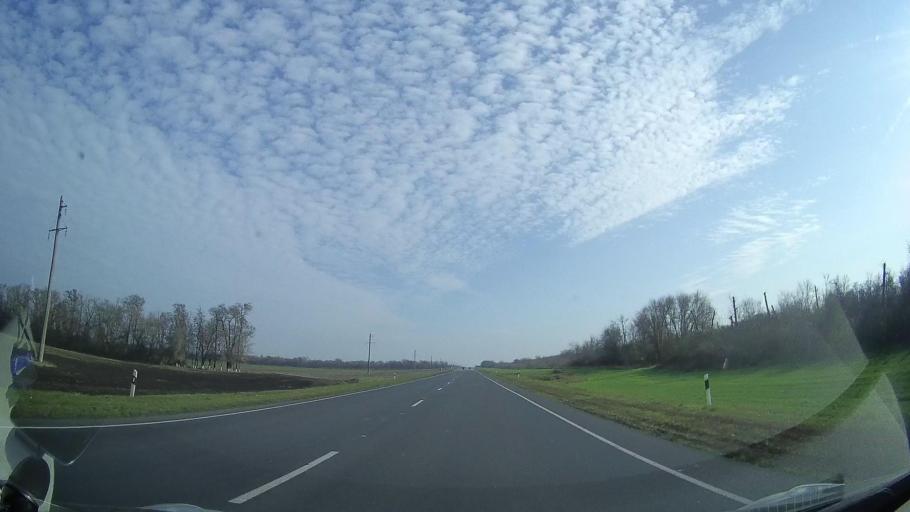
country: RU
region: Rostov
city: Gigant
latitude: 46.5268
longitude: 41.2209
